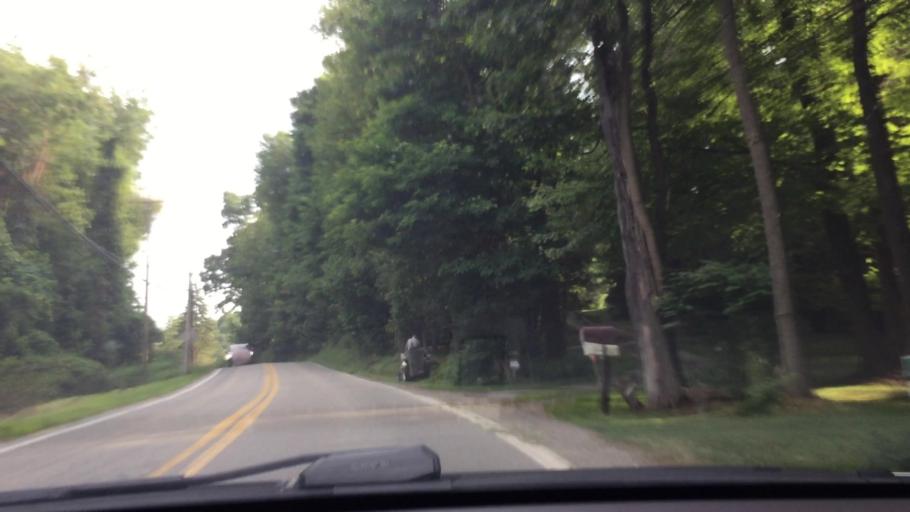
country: US
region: Pennsylvania
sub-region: Butler County
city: Seven Fields
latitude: 40.6726
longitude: -80.0696
